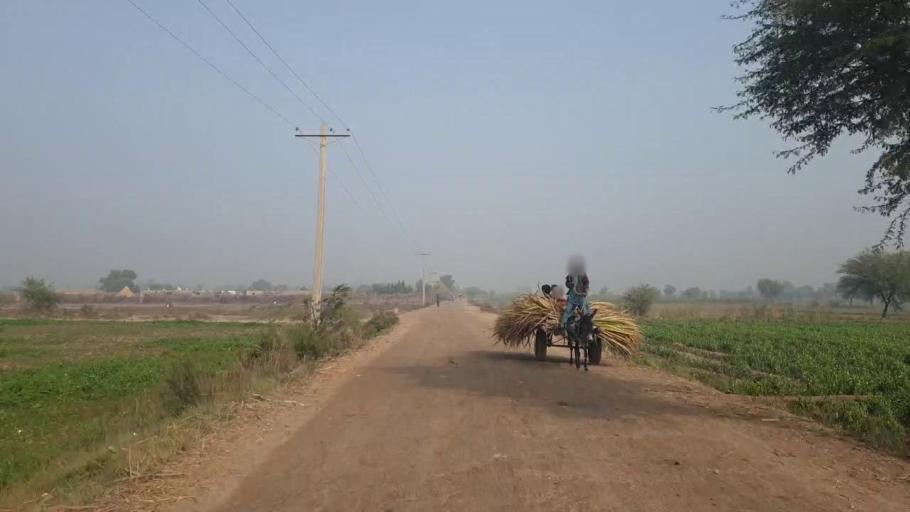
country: PK
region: Sindh
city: Tando Adam
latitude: 25.8065
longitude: 68.6133
